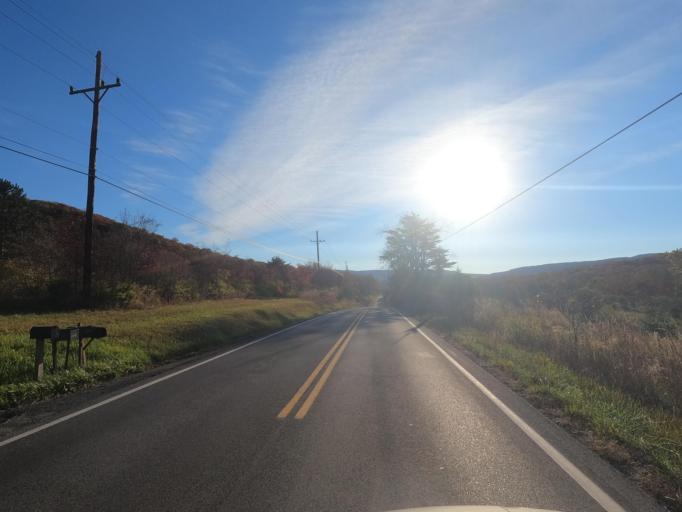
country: US
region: West Virginia
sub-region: Mineral County
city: Fort Ashby
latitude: 39.5419
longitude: -78.4927
